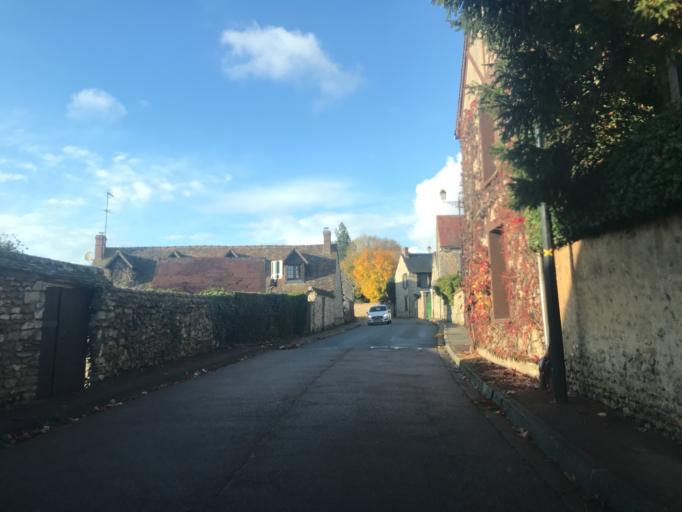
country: FR
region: Haute-Normandie
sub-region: Departement de l'Eure
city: Houlbec-Cocherel
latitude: 49.0756
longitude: 1.3061
